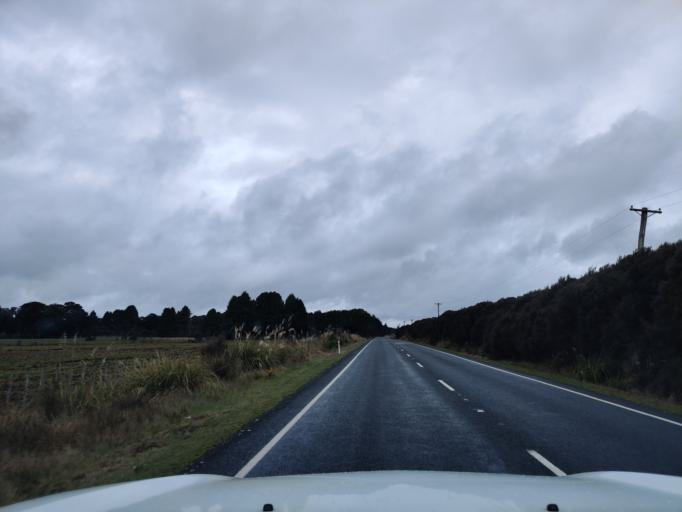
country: NZ
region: Manawatu-Wanganui
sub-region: Ruapehu District
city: Waiouru
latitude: -39.3378
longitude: 175.3795
